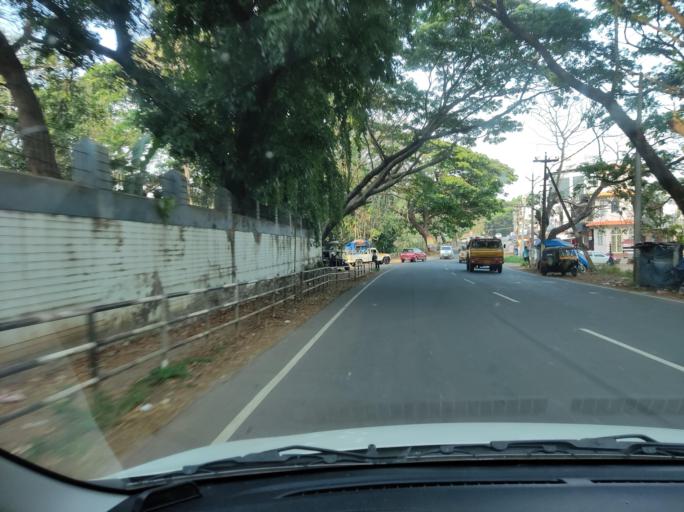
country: IN
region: Kerala
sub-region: Kottayam
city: Kottayam
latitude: 9.6349
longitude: 76.5258
